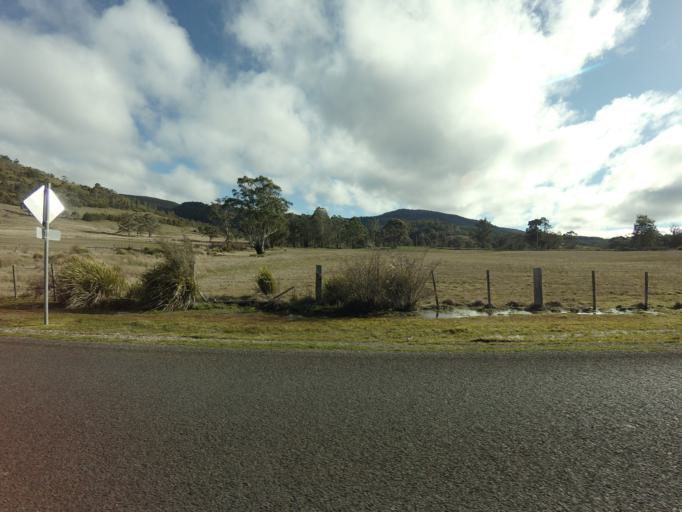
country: AU
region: Tasmania
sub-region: Derwent Valley
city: New Norfolk
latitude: -42.6054
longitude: 146.7059
